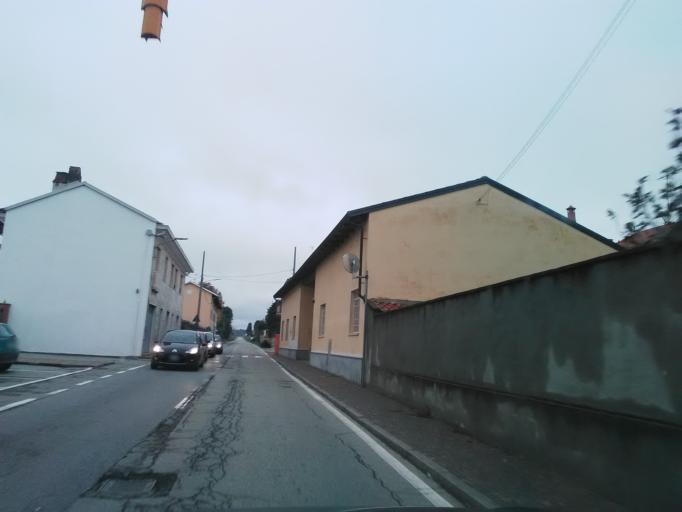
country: IT
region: Piedmont
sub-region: Provincia di Vercelli
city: Cigliano
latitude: 45.3096
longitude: 8.0152
